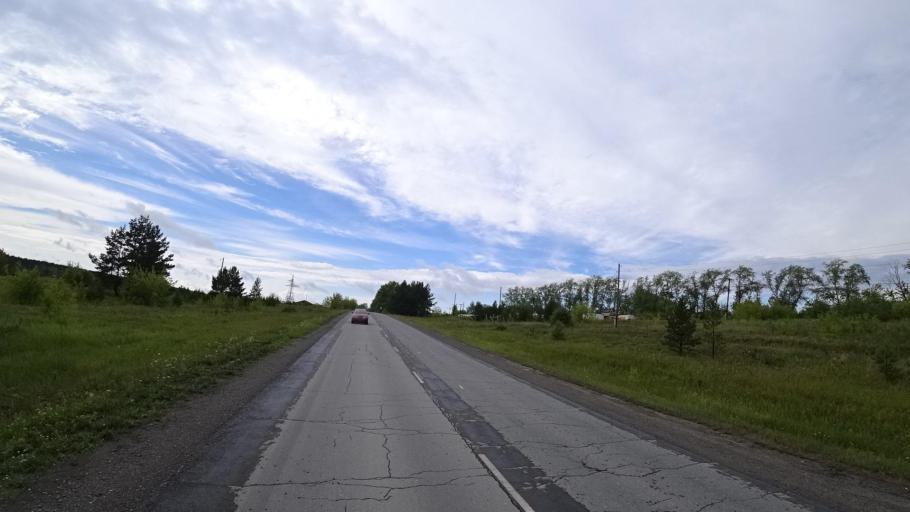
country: RU
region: Sverdlovsk
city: Kamyshlov
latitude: 56.8437
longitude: 62.7733
